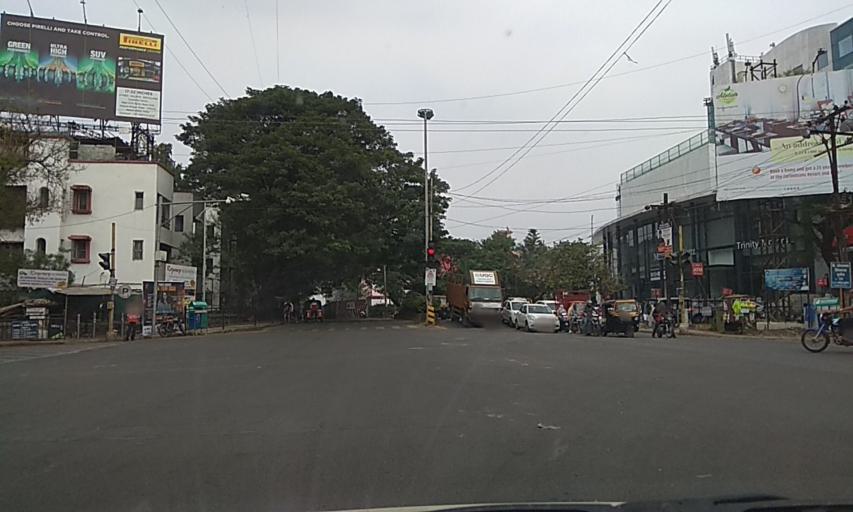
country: IN
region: Maharashtra
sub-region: Pune Division
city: Shivaji Nagar
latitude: 18.5458
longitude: 73.9060
